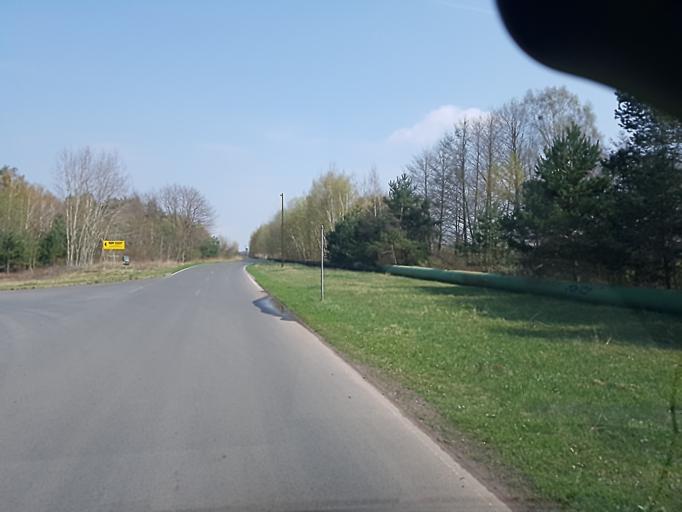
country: DE
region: Saxony-Anhalt
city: Grafenhainichen
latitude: 51.7468
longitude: 12.4336
